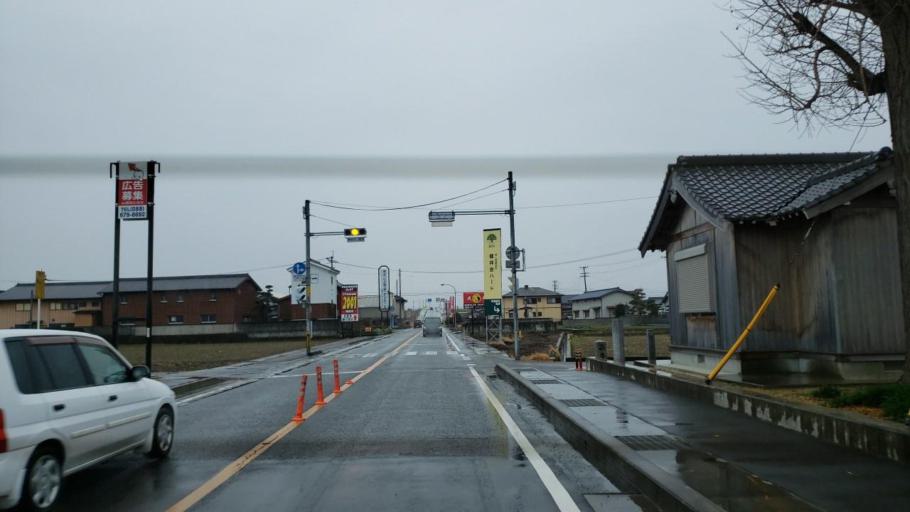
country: JP
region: Tokushima
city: Ishii
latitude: 34.1124
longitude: 134.4364
